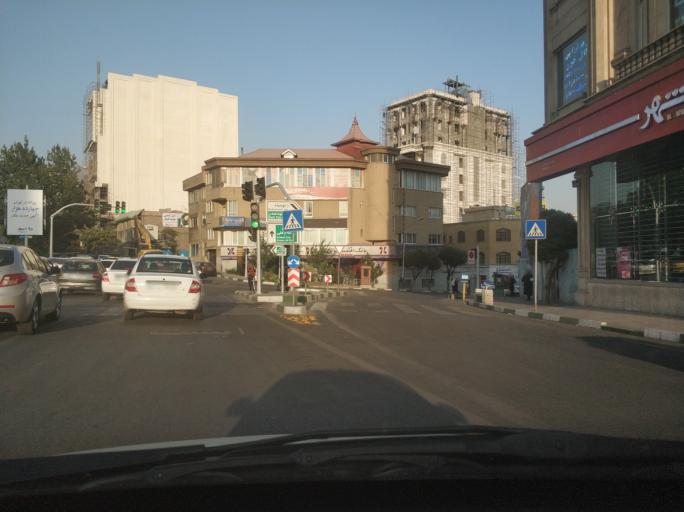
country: IR
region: Tehran
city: Tajrish
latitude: 35.7988
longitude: 51.4743
